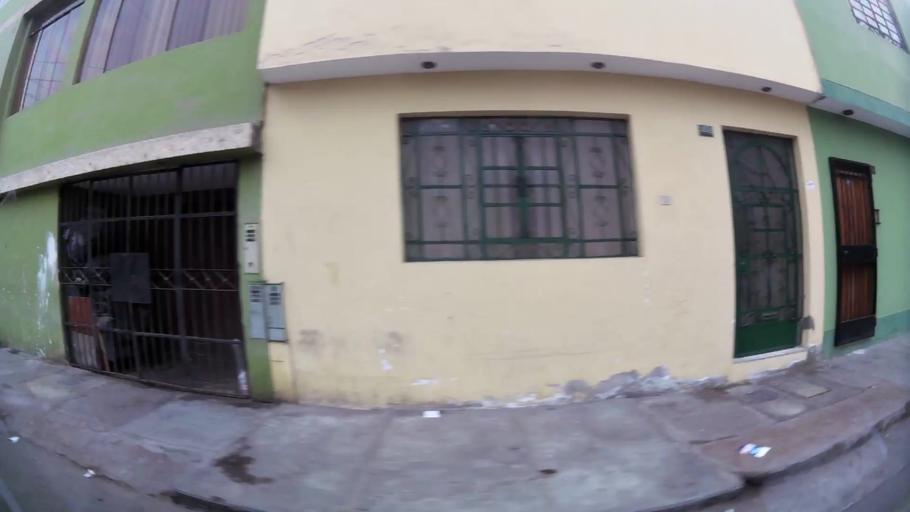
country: PE
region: Lima
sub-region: Lima
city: Surco
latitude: -12.1625
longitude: -76.9766
